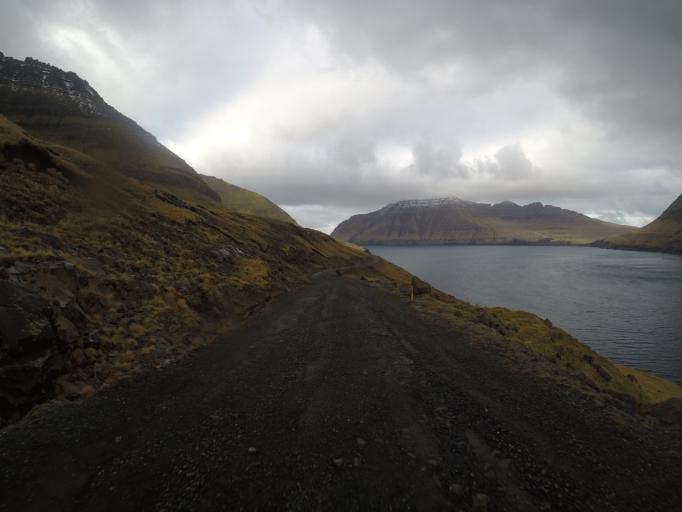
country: FO
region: Nordoyar
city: Klaksvik
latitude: 62.3400
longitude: -6.5806
